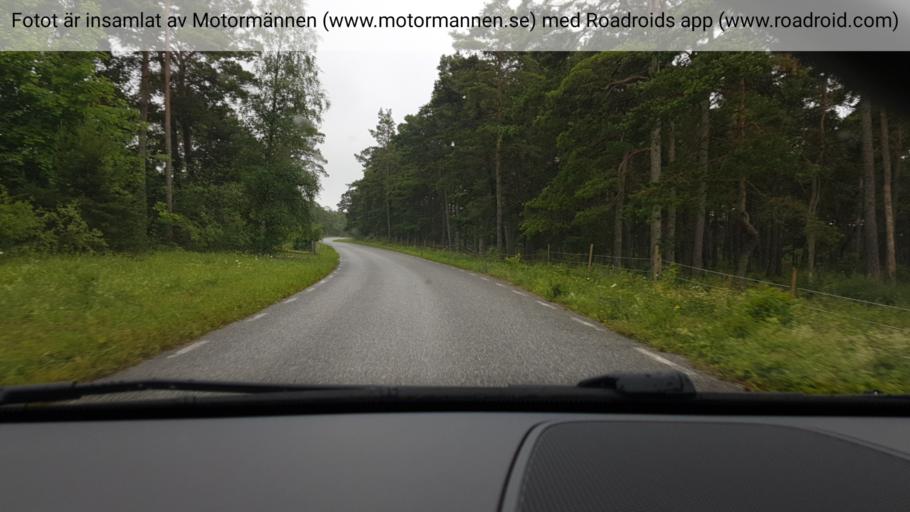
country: SE
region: Gotland
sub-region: Gotland
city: Slite
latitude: 57.8668
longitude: 18.8682
